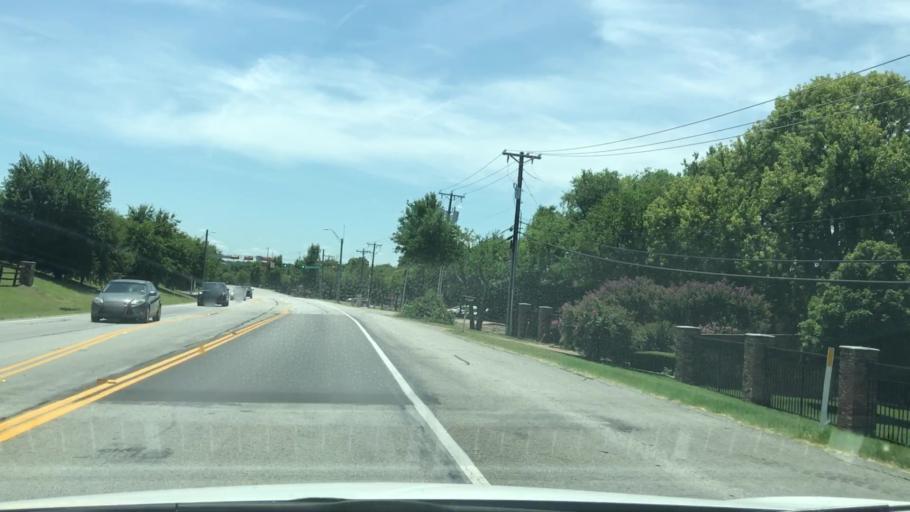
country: US
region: Texas
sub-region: Rockwall County
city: Rockwall
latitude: 32.9589
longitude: -96.4647
